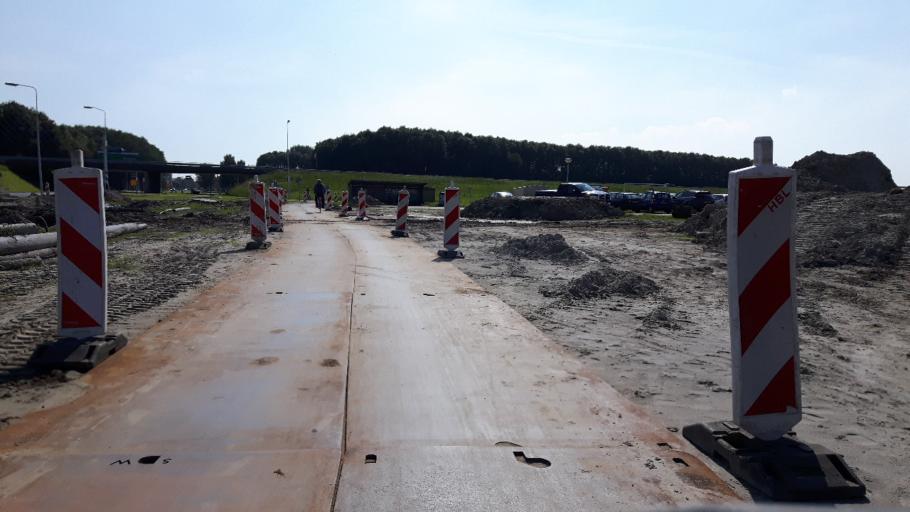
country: NL
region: Friesland
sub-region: Gemeente Franekeradeel
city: Franeker
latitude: 53.2023
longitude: 5.5414
